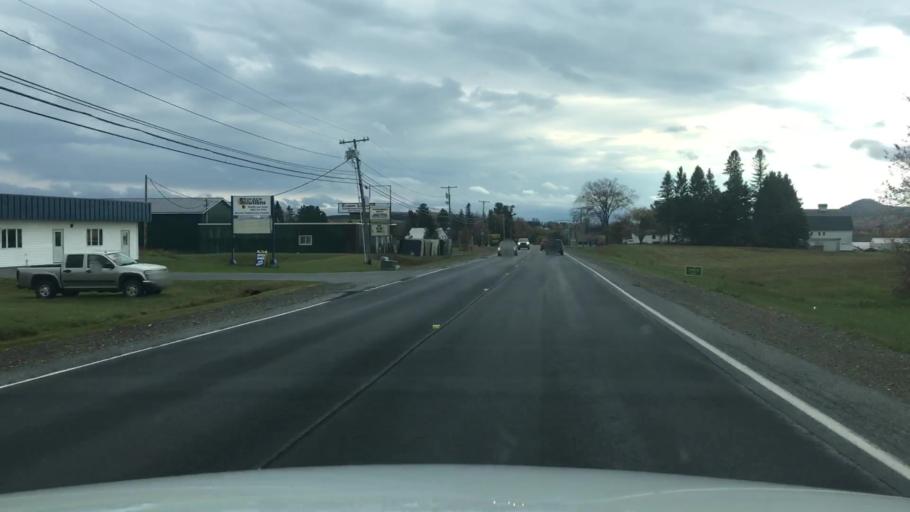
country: US
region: Maine
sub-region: Aroostook County
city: Presque Isle
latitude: 46.6574
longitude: -68.0066
